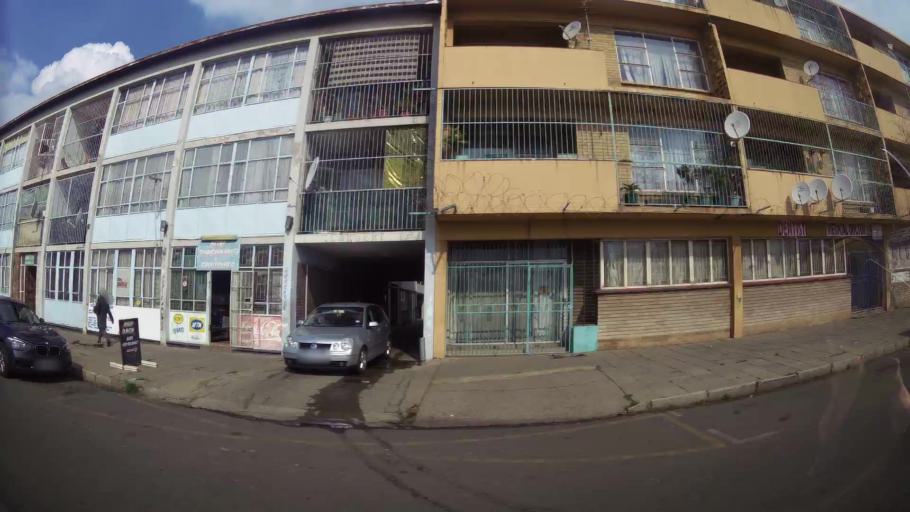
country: ZA
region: Gauteng
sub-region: Sedibeng District Municipality
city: Vereeniging
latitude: -26.6716
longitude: 27.9282
